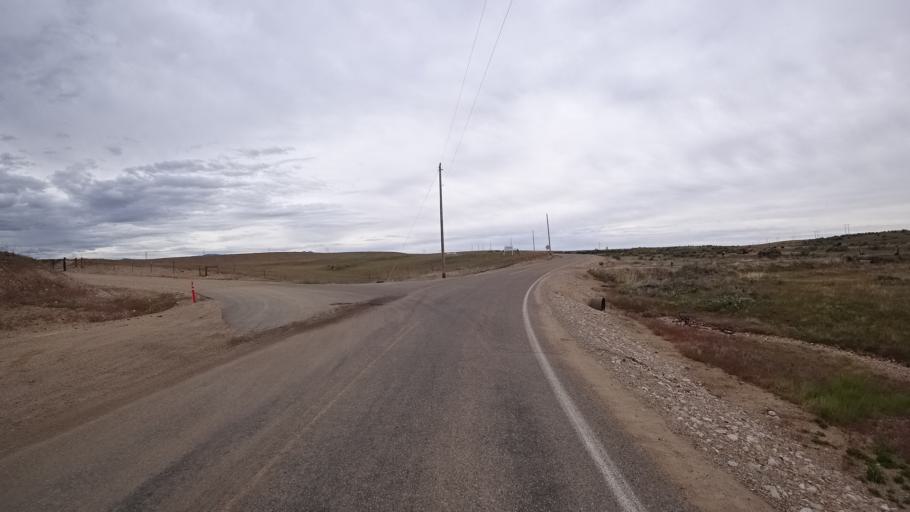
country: US
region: Idaho
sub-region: Ada County
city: Boise
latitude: 43.4691
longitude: -116.0757
